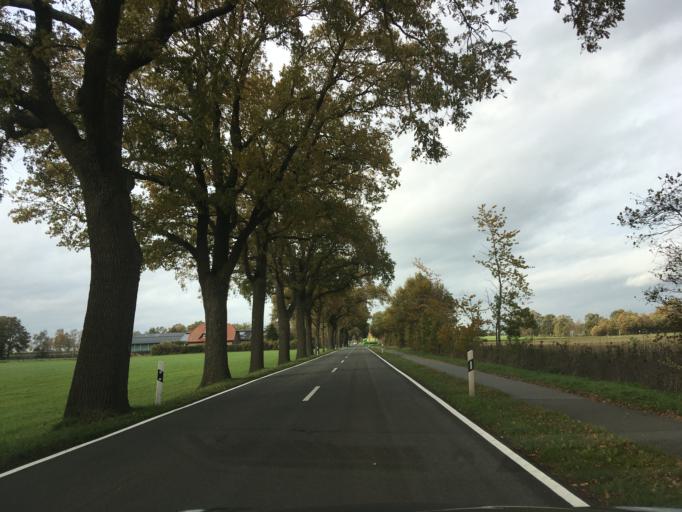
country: DE
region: North Rhine-Westphalia
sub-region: Regierungsbezirk Munster
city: Vreden
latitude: 52.0961
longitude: 6.8862
